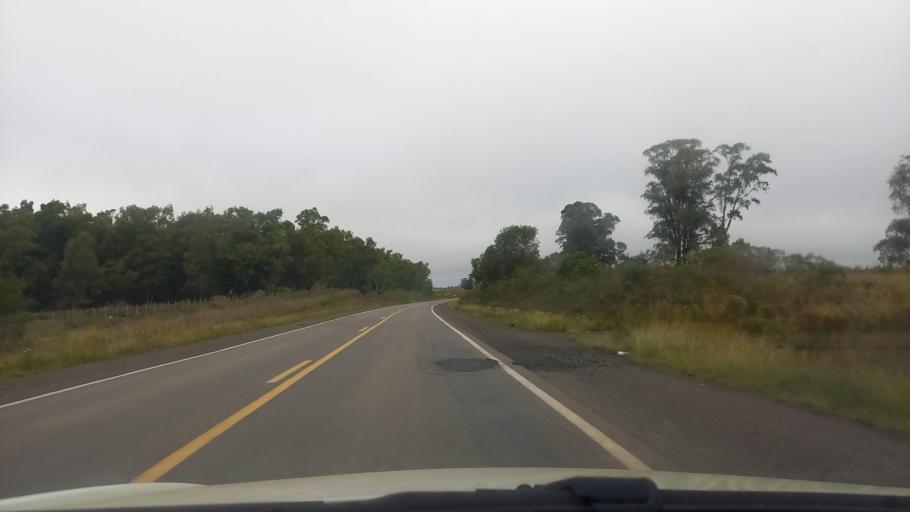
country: BR
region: Rio Grande do Sul
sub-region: Cacequi
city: Cacequi
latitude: -30.0629
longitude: -54.6081
